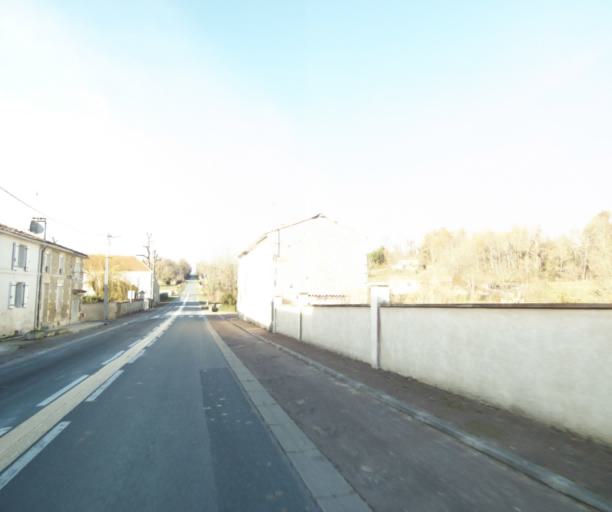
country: FR
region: Poitou-Charentes
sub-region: Departement de la Charente-Maritime
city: Burie
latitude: 45.7948
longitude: -0.4408
